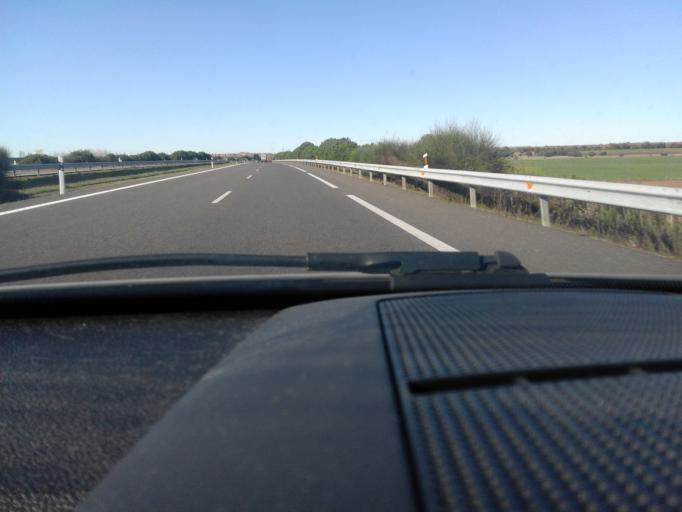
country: ES
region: Castille and Leon
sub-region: Provincia de Leon
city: Calzada del Coto
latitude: 42.3873
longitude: -5.1031
